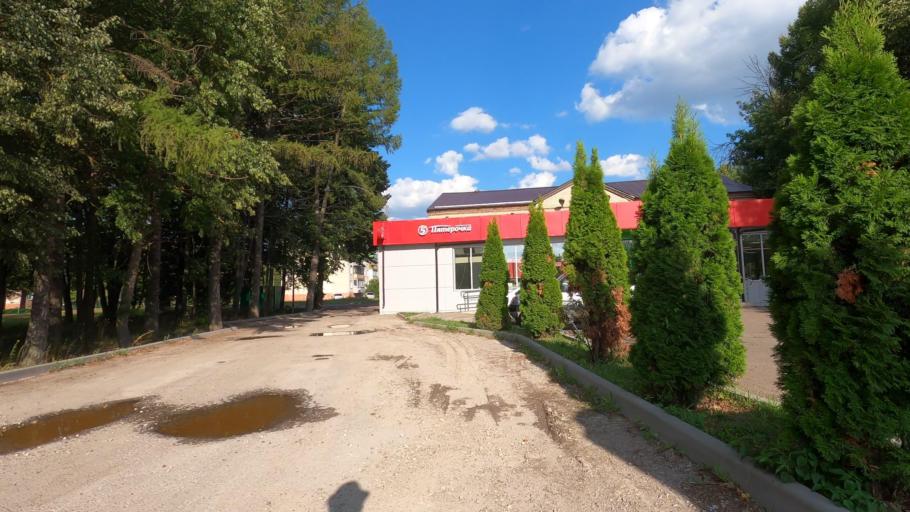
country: RU
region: Moskovskaya
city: Peski
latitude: 55.1938
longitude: 38.7406
